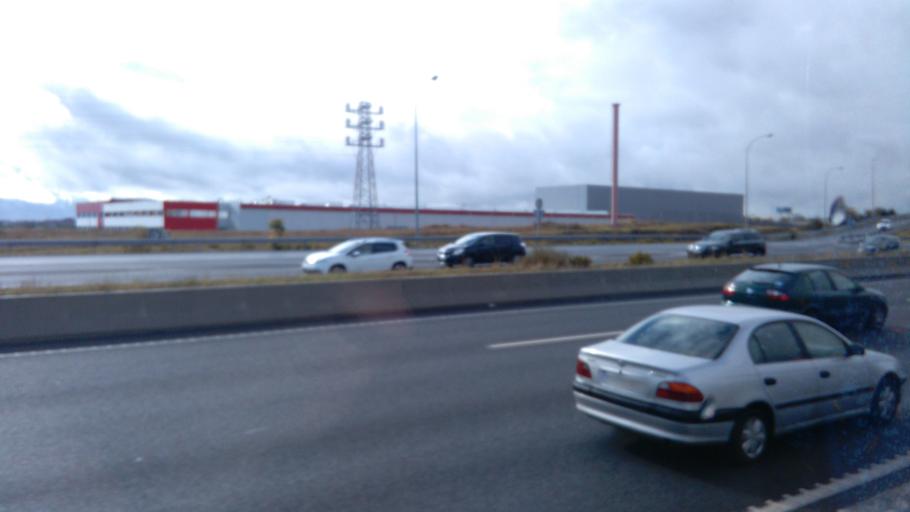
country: ES
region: Madrid
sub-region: Provincia de Madrid
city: Latina
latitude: 40.3622
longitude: -3.7376
